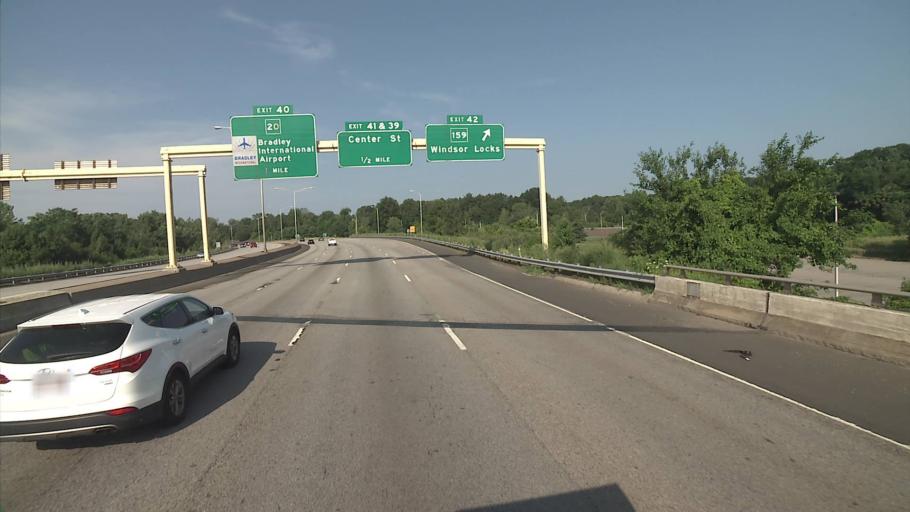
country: US
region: Connecticut
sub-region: Hartford County
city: Windsor Locks
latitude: 41.9163
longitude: -72.6262
